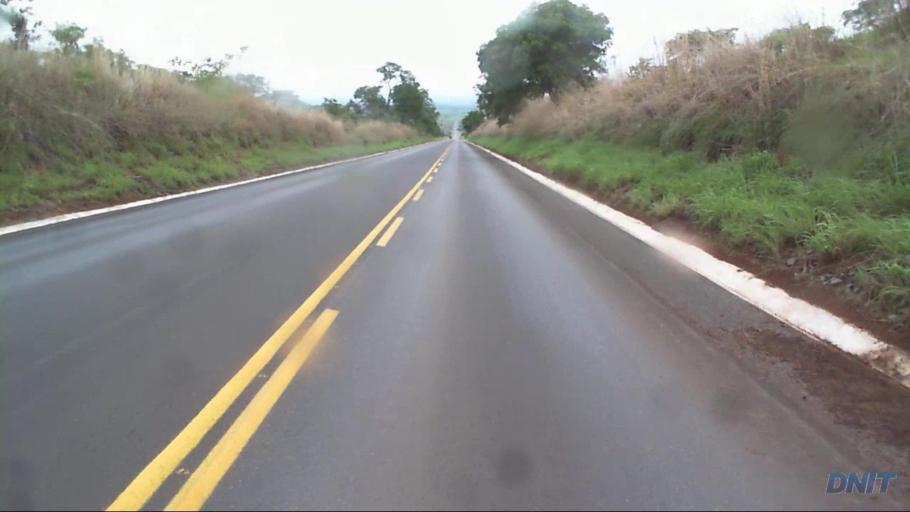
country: BR
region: Goias
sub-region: Padre Bernardo
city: Padre Bernardo
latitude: -15.1786
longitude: -48.4190
